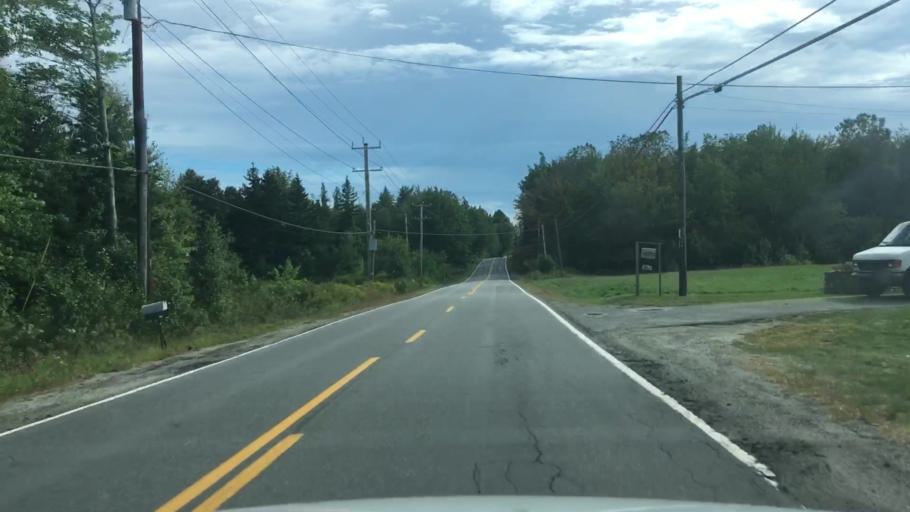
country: US
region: Maine
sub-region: Hancock County
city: Ellsworth
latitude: 44.4855
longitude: -68.4202
